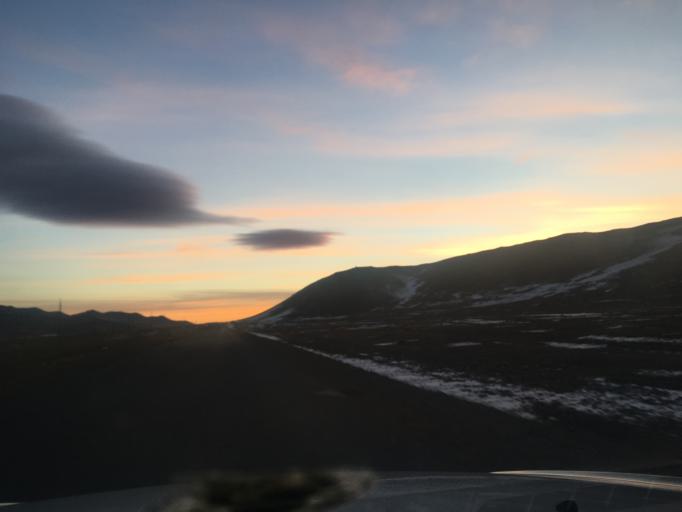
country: MN
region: Central Aimak
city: Mandal
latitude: 48.1153
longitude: 106.6424
